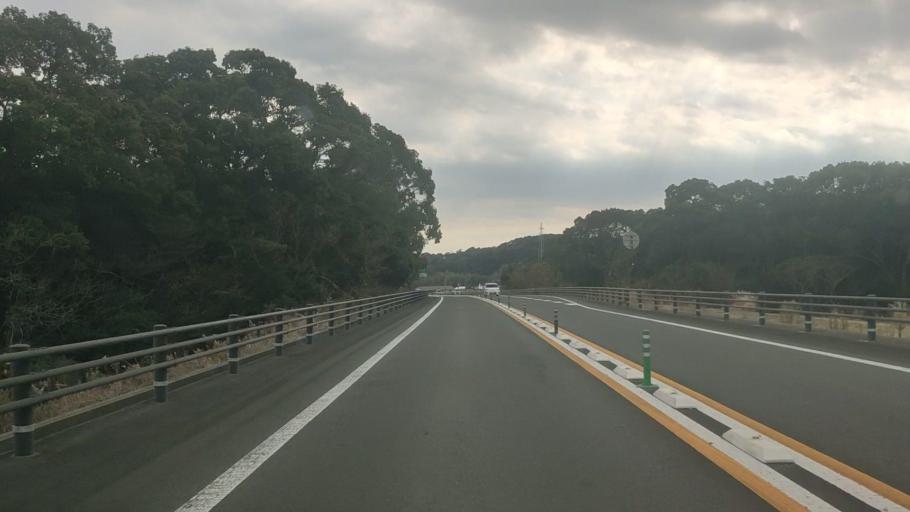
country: JP
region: Nagasaki
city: Shimabara
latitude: 32.7658
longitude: 130.3603
